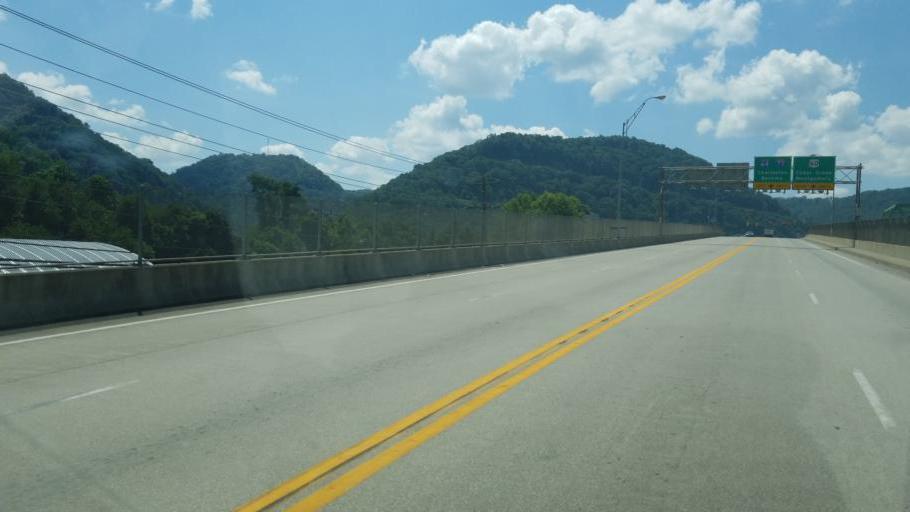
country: US
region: West Virginia
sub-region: Kanawha County
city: Chesapeake
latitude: 38.1959
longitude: -81.4941
